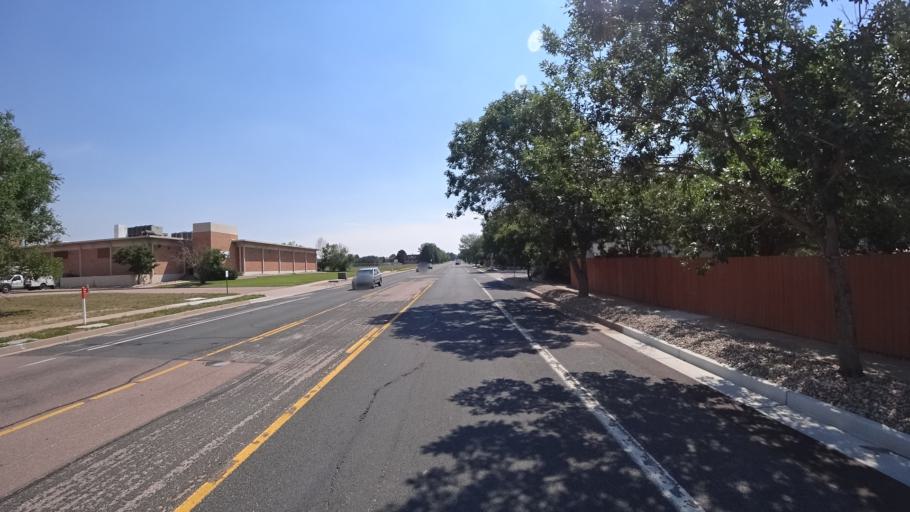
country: US
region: Colorado
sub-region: El Paso County
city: Air Force Academy
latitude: 38.9257
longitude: -104.8095
